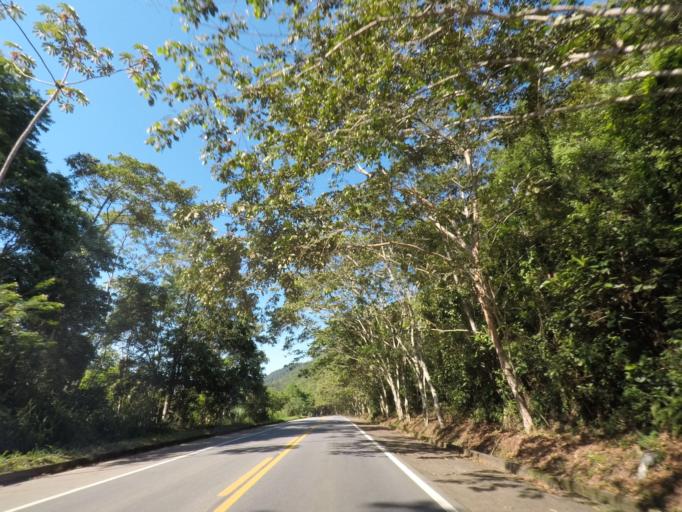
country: BR
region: Rio de Janeiro
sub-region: Parati
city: Paraty
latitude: -23.2744
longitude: -44.6879
